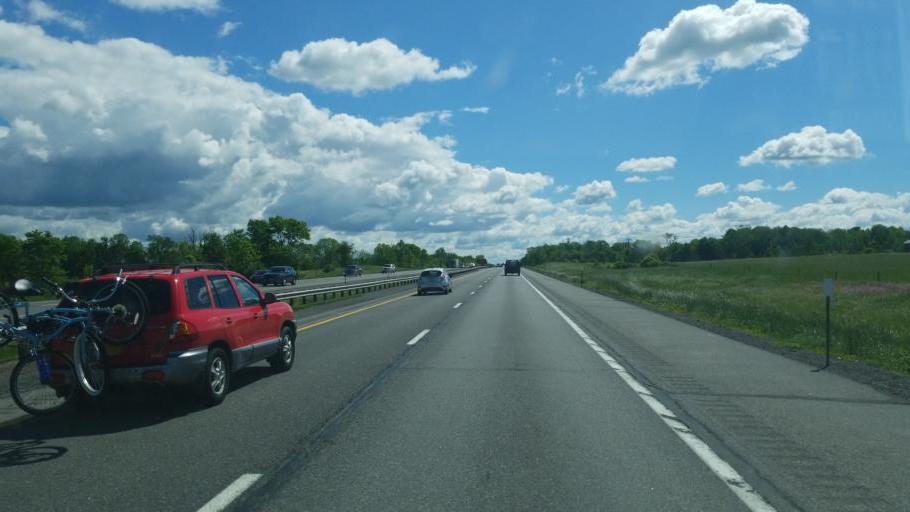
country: US
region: New York
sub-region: Oneida County
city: Vernon
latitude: 43.1285
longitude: -75.5446
